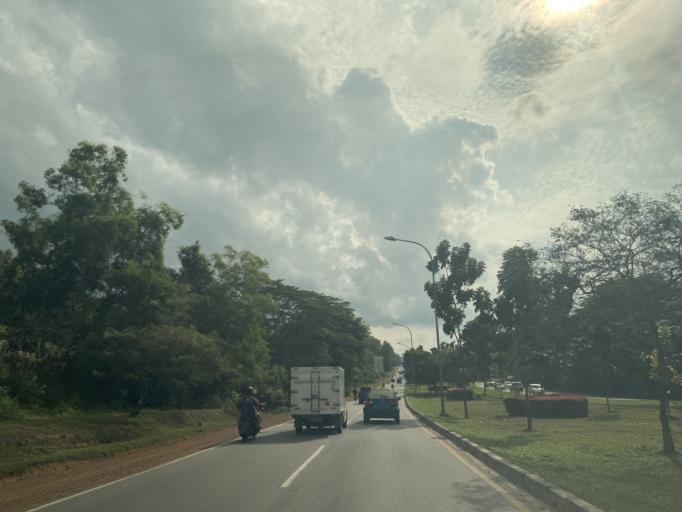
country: SG
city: Singapore
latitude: 1.0988
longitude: 104.0657
